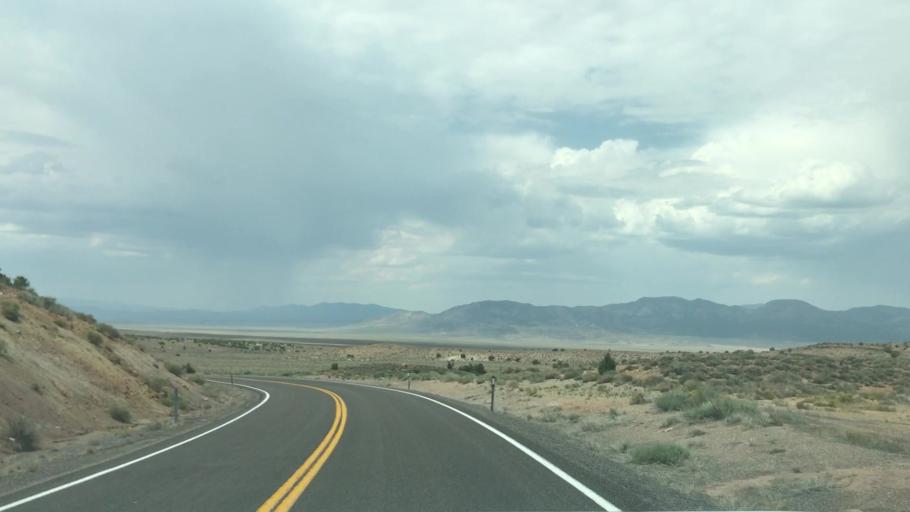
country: US
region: Nevada
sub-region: Eureka County
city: Eureka
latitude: 39.3998
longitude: -115.7087
